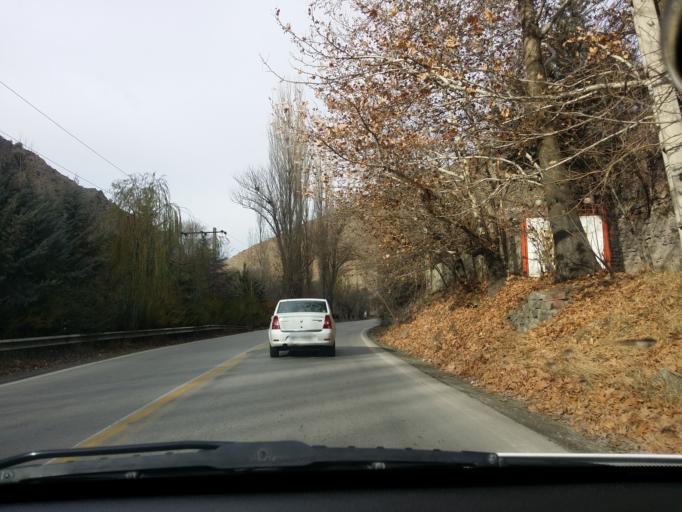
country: IR
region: Tehran
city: Tajrish
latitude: 36.0242
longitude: 51.2582
